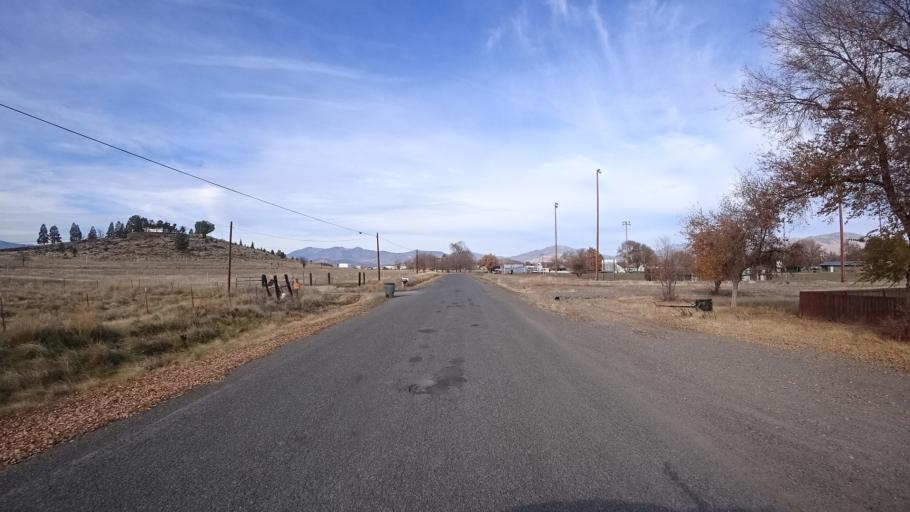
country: US
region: California
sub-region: Siskiyou County
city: Montague
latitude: 41.7216
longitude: -122.5262
